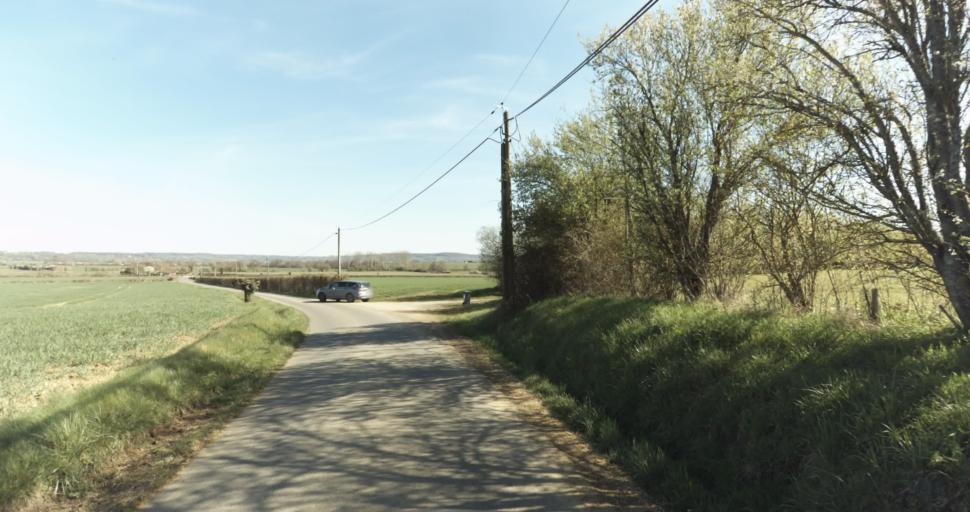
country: FR
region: Lower Normandy
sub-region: Departement du Calvados
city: Saint-Pierre-sur-Dives
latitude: 49.0491
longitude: -0.0180
